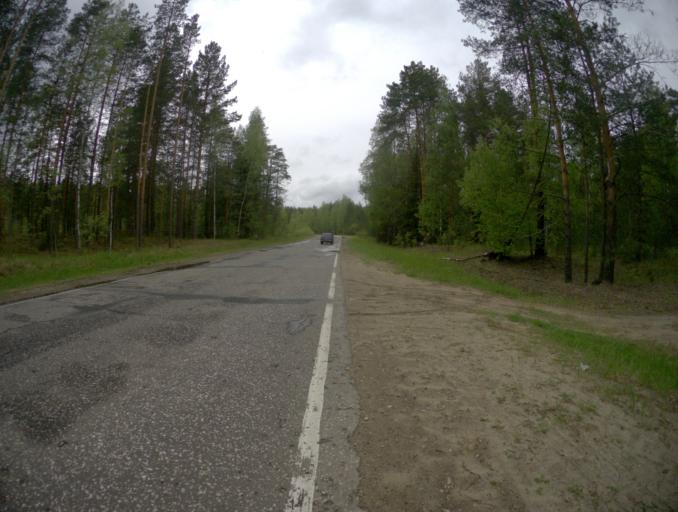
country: RU
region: Vladimir
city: Velikodvorskiy
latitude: 55.3957
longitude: 40.7058
